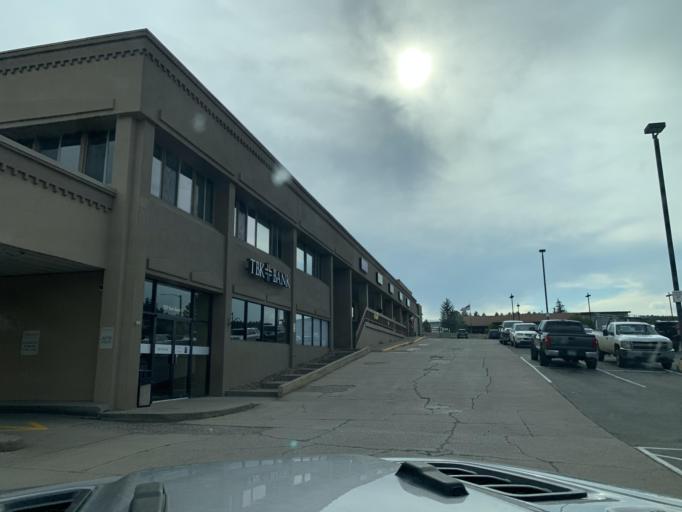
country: US
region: Colorado
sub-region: Archuleta County
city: Pagosa Springs
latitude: 37.2661
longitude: -107.0159
